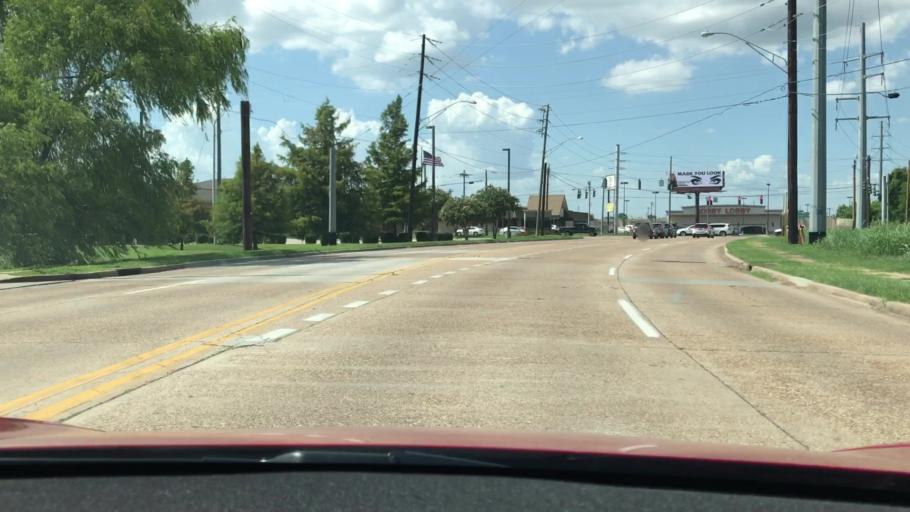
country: US
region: Louisiana
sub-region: Bossier Parish
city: Bossier City
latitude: 32.4423
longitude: -93.7135
